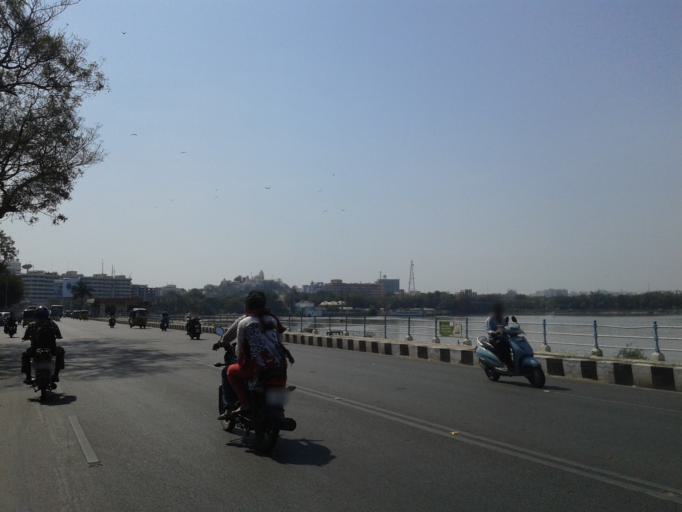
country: IN
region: Telangana
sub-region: Hyderabad
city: Hyderabad
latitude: 17.4128
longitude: 78.4780
